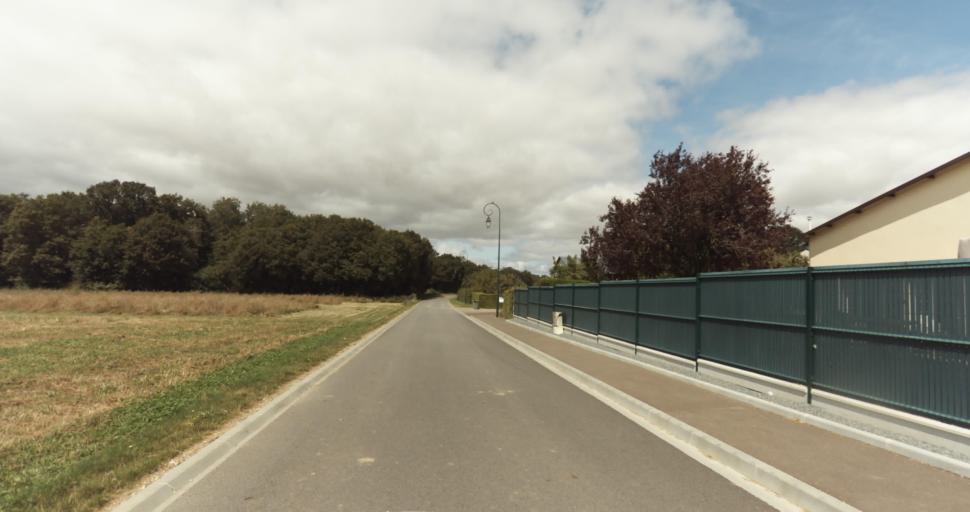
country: FR
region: Haute-Normandie
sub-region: Departement de l'Eure
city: Evreux
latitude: 48.9165
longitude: 1.2065
